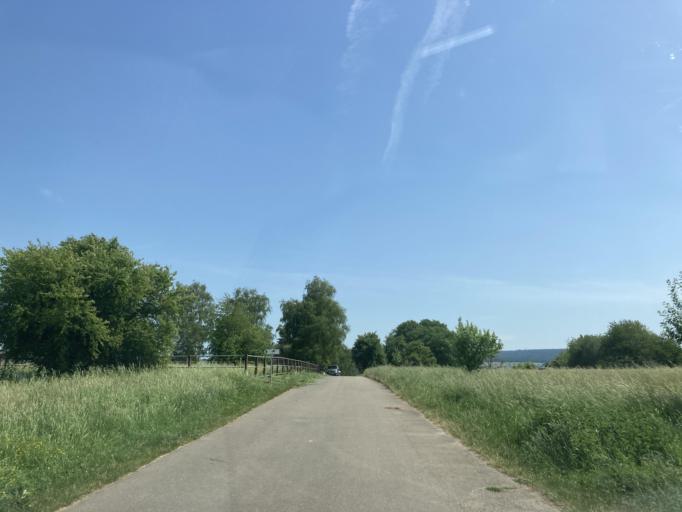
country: DE
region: Baden-Wuerttemberg
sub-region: Karlsruhe Region
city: Dobel
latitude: 48.8713
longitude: 8.5034
